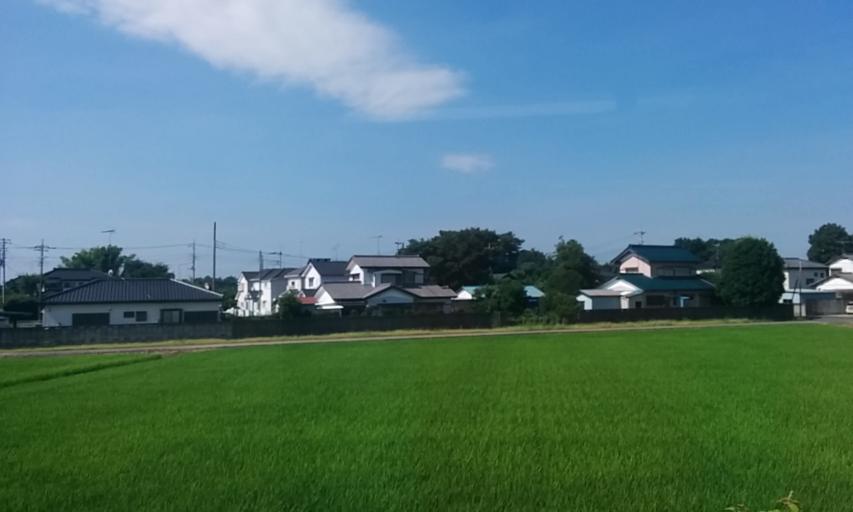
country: JP
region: Saitama
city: Kazo
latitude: 36.1414
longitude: 139.5687
